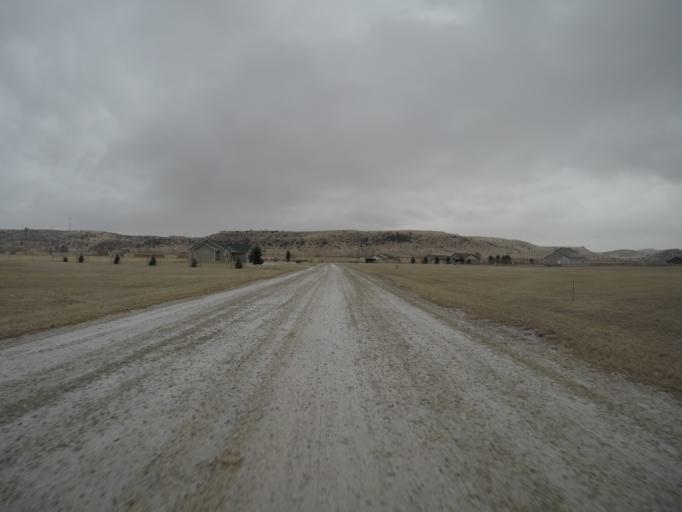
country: US
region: Montana
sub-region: Stillwater County
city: Absarokee
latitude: 45.5283
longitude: -109.4653
